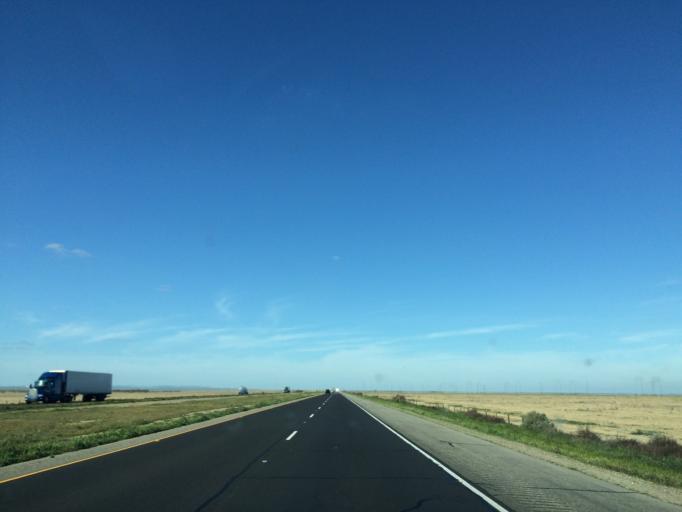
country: US
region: California
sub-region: Kern County
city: Lost Hills
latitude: 35.8101
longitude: -119.7974
